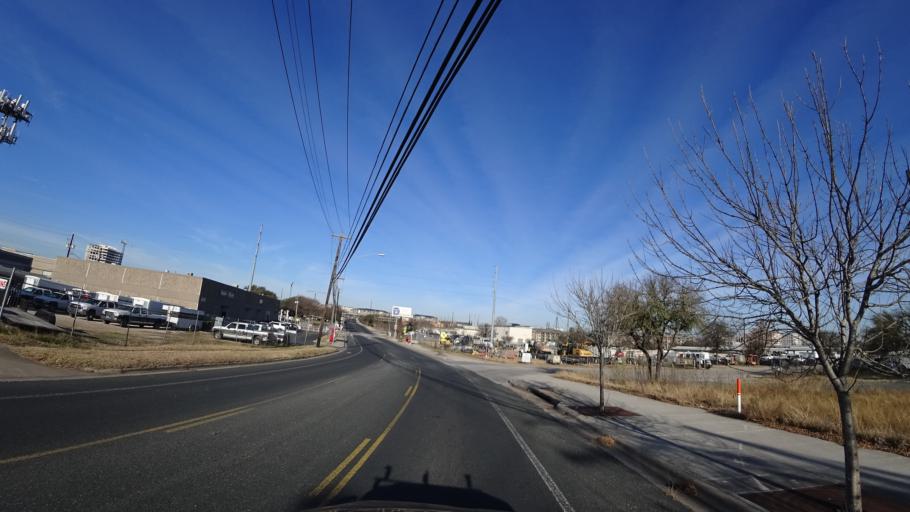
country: US
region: Texas
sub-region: Travis County
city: Wells Branch
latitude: 30.3927
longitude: -97.7151
